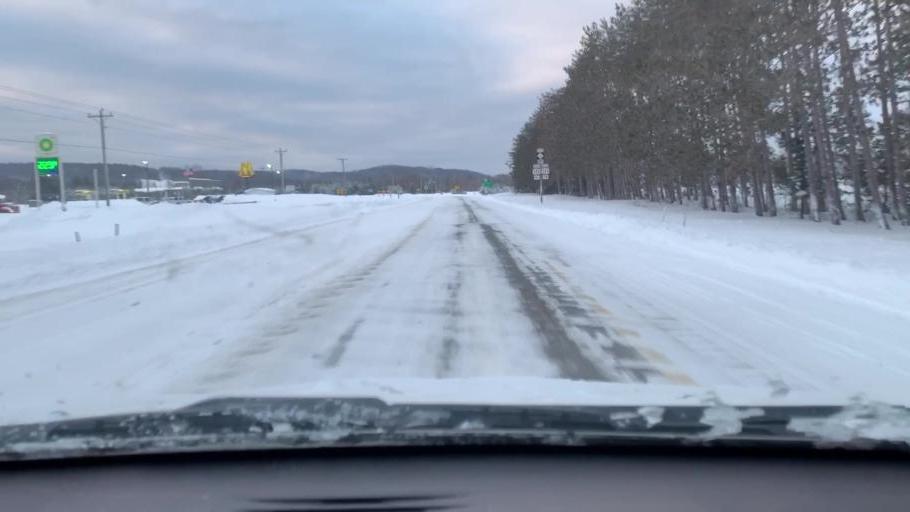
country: US
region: Michigan
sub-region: Antrim County
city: Mancelona
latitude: 44.9145
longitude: -85.0510
